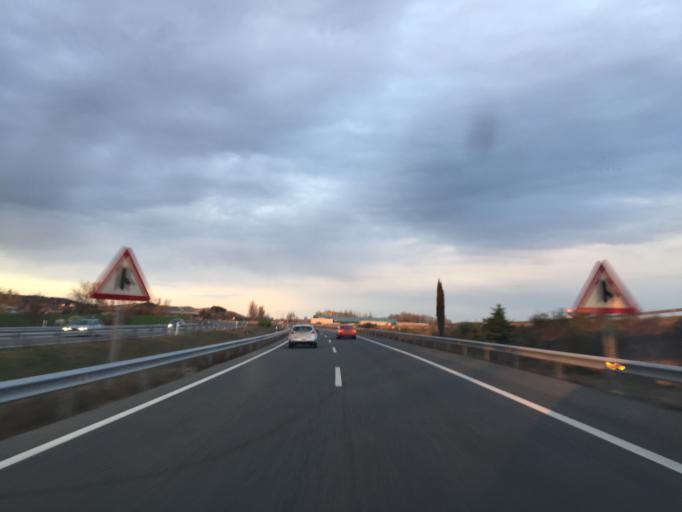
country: ES
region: Castille and Leon
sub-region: Provincia de Burgos
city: Estepar
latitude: 42.2739
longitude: -3.8966
